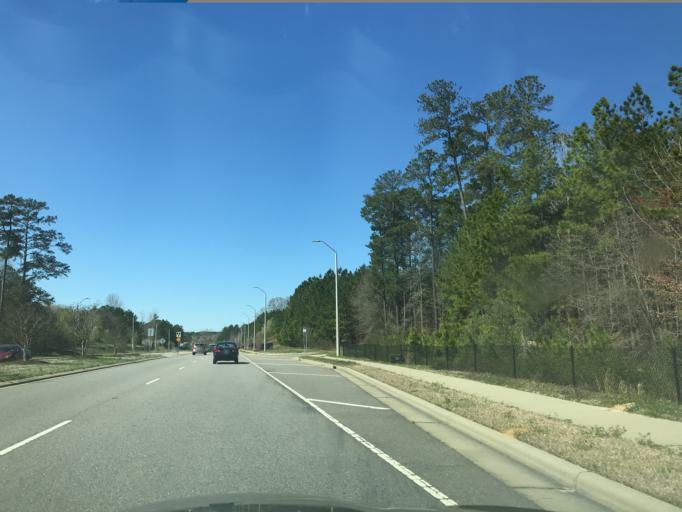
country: US
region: North Carolina
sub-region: Wake County
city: Garner
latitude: 35.6885
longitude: -78.5874
